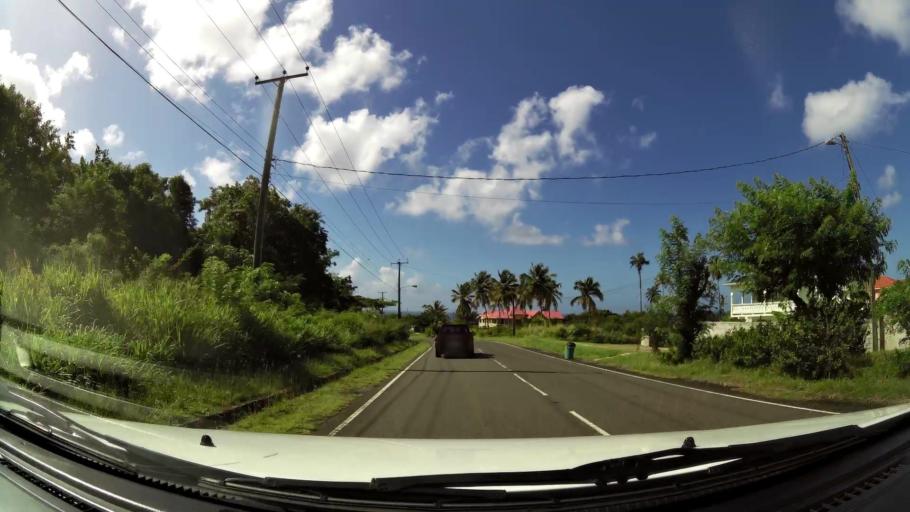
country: LC
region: Choiseul Quarter
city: Choiseul
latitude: 13.7678
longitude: -61.0347
